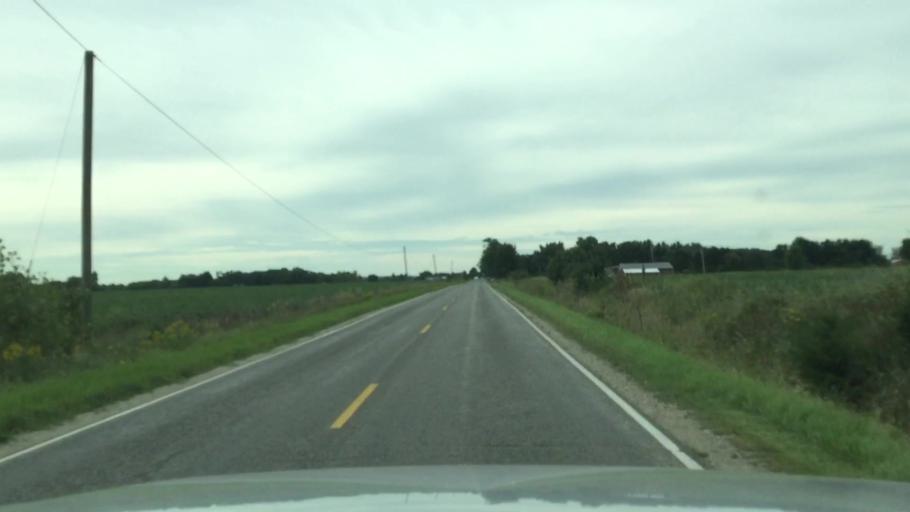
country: US
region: Michigan
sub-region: Genesee County
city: Flushing
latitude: 43.0494
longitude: -83.9874
